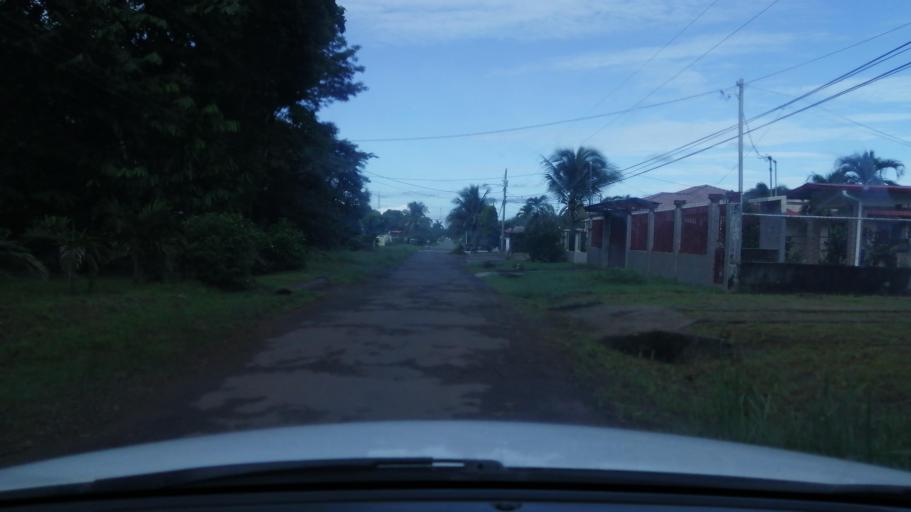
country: PA
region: Chiriqui
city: El Quiteno
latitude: 8.4691
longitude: -82.4128
